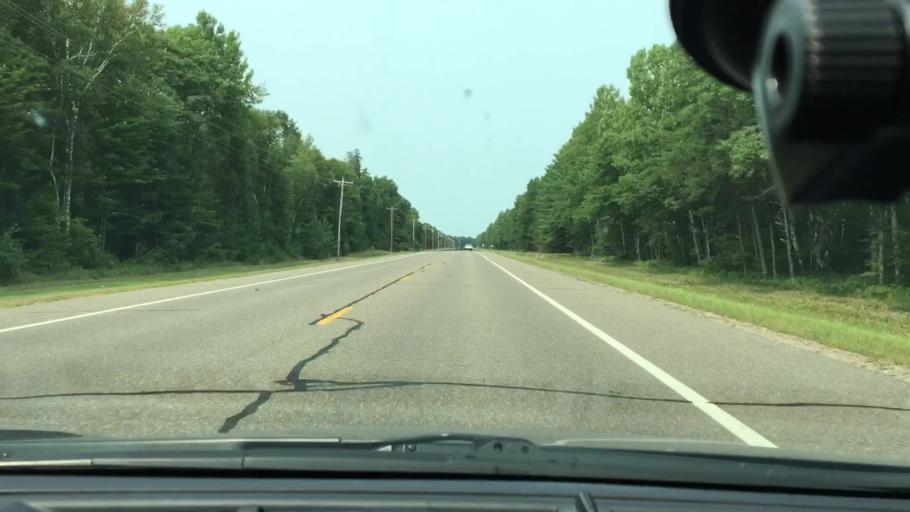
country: US
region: Minnesota
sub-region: Crow Wing County
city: Breezy Point
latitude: 46.5473
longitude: -94.1358
